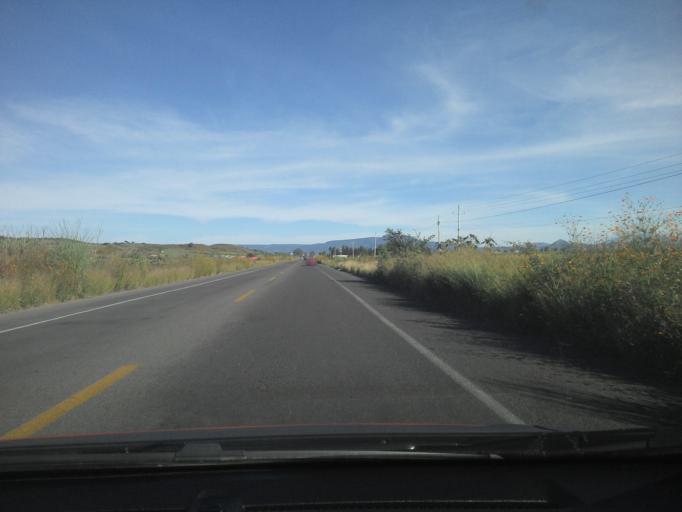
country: MX
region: Jalisco
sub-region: Teuchitlan
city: La Estanzuela
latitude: 20.6699
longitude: -103.8055
